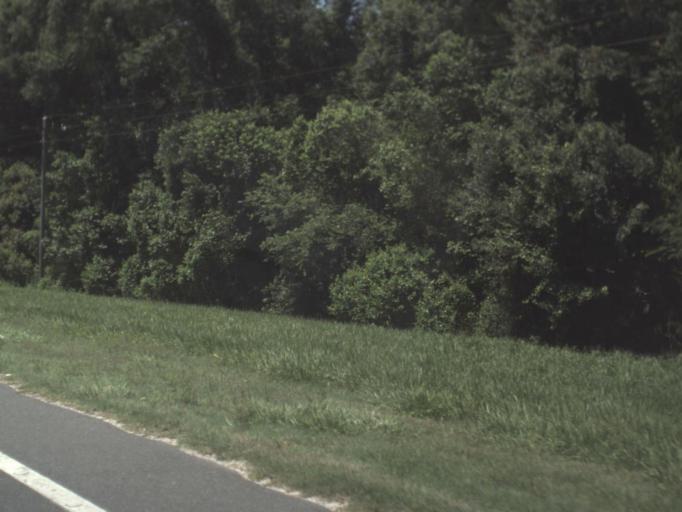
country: US
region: Florida
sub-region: Lafayette County
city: Mayo
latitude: 30.0591
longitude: -83.1871
